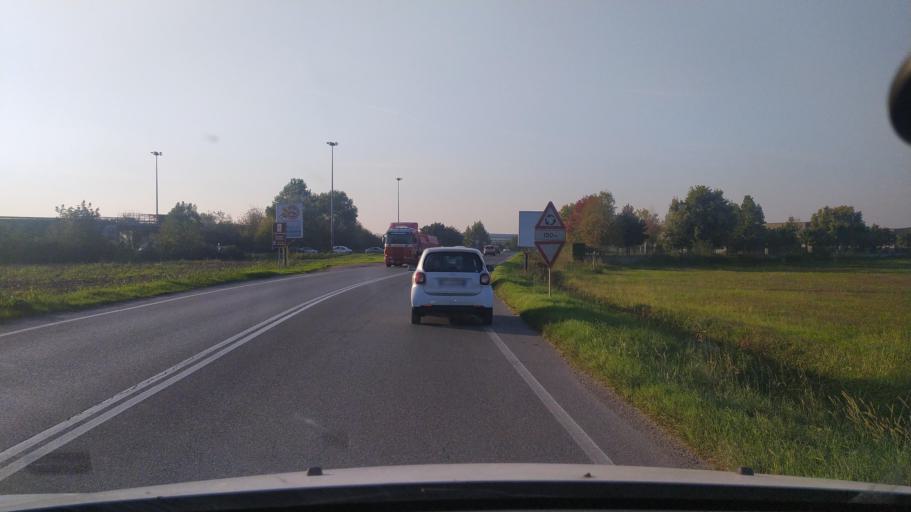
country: IT
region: Lombardy
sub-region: Provincia di Cremona
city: Capergnanica
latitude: 45.3617
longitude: 9.6381
